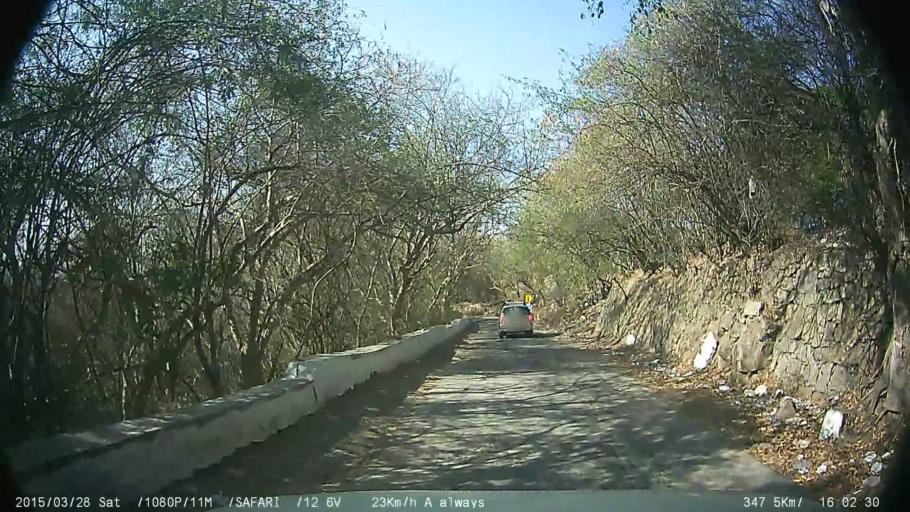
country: IN
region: Karnataka
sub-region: Mysore
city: Mysore
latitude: 12.2791
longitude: 76.6676
